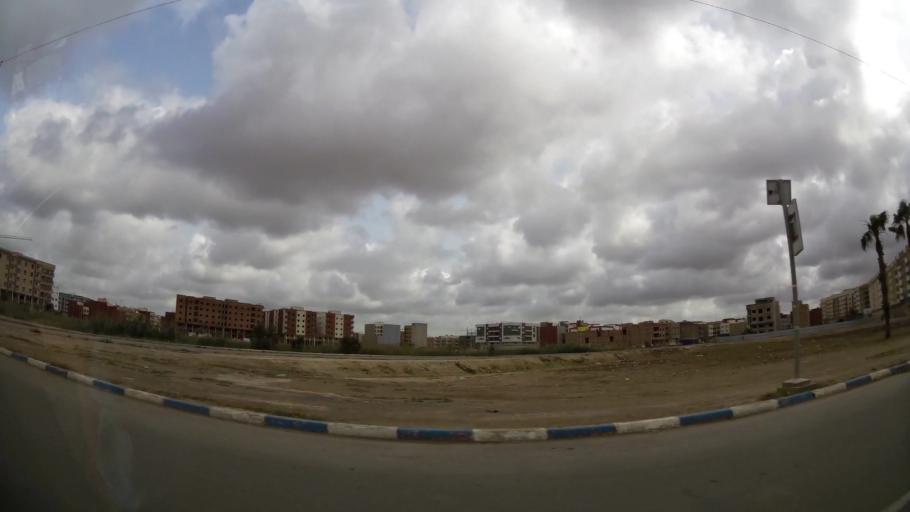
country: MA
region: Oriental
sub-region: Nador
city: Nador
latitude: 35.1535
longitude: -2.9131
